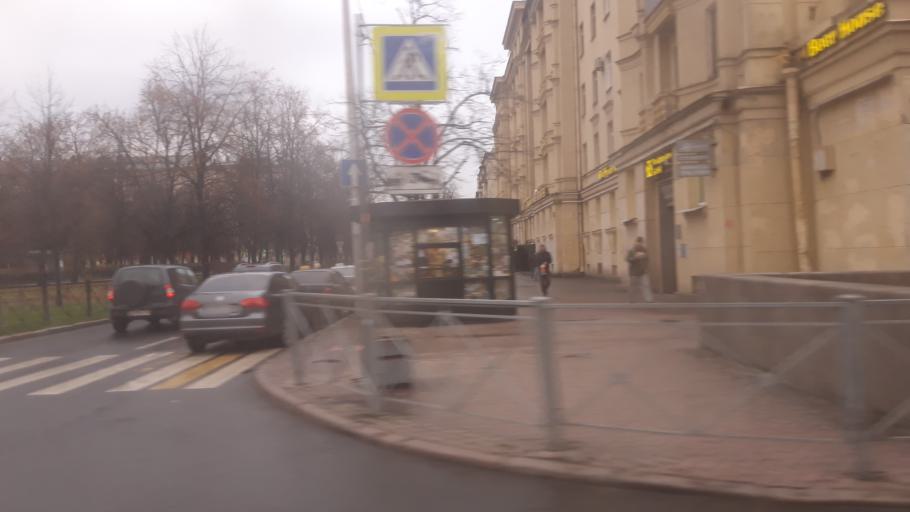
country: RU
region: St.-Petersburg
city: Kupchino
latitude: 59.8492
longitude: 30.3218
